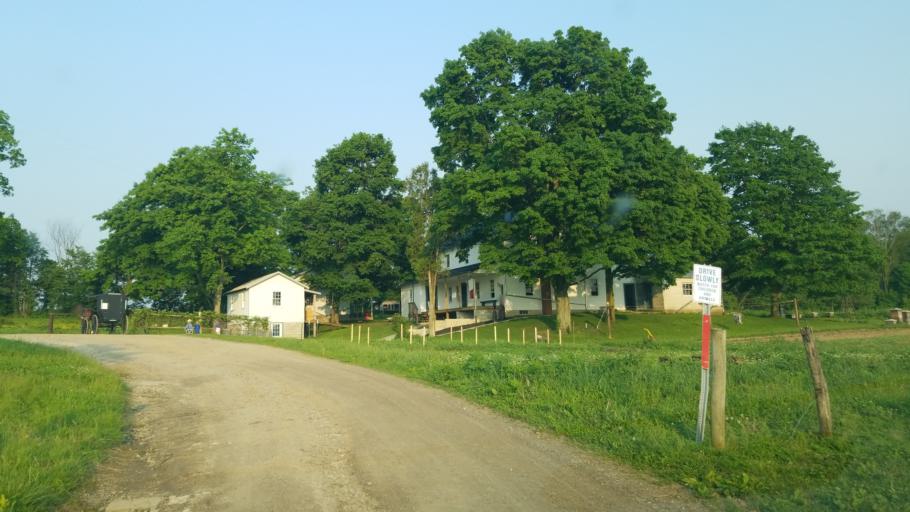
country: US
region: Ohio
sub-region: Wayne County
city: West Salem
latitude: 40.9257
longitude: -82.1016
